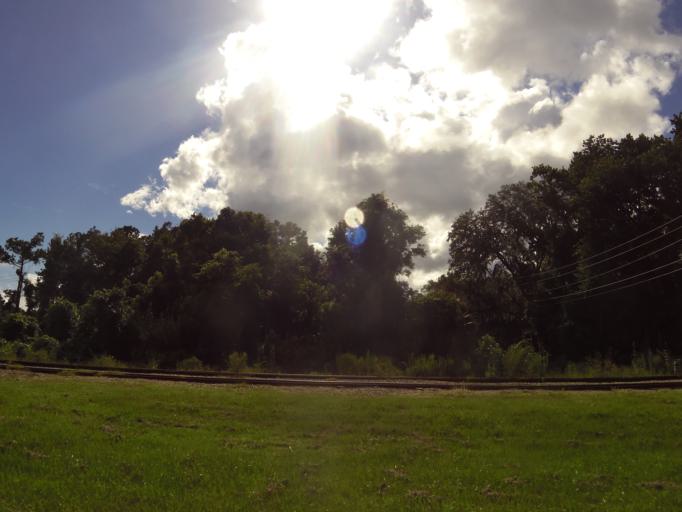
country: US
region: Georgia
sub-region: Camden County
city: Kingsland
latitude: 30.8009
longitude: -81.6913
